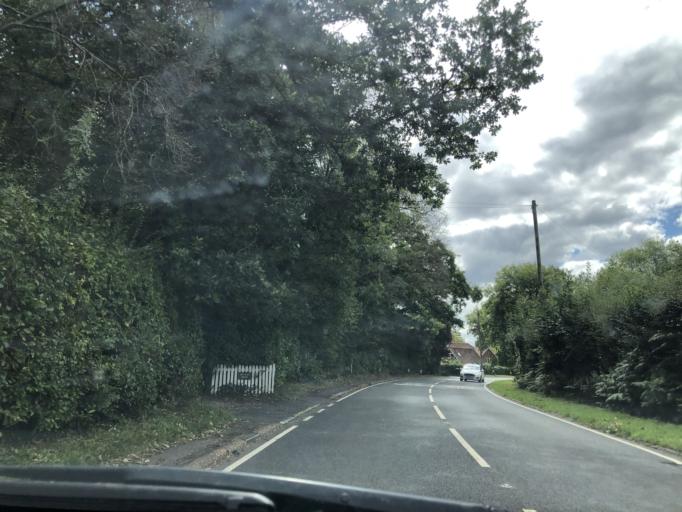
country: GB
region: England
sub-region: East Sussex
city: Forest Row
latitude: 51.0899
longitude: 0.0868
